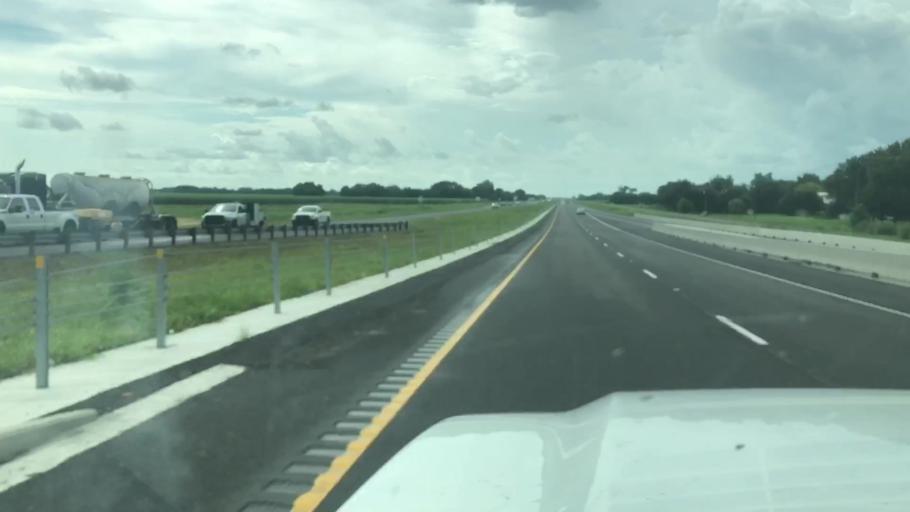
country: US
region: Louisiana
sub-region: Iberia Parish
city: Jeanerette
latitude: 29.8680
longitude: -91.6362
